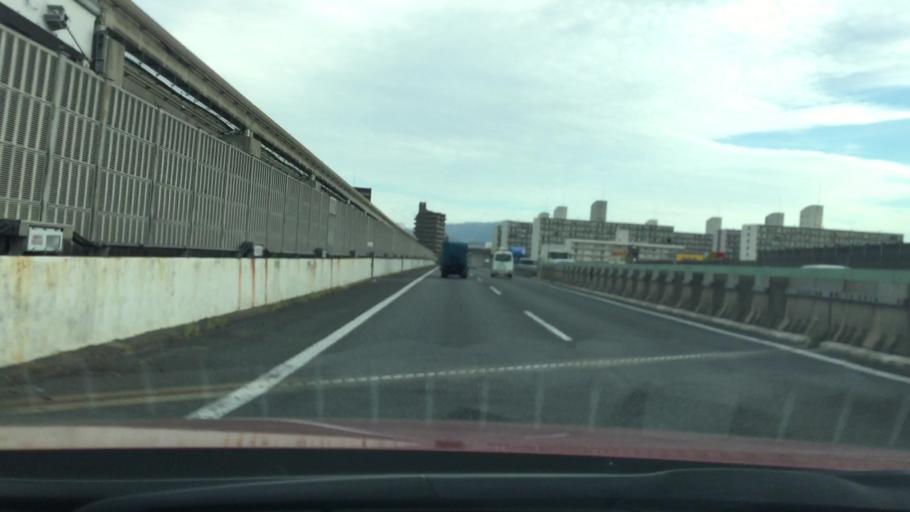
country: JP
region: Osaka
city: Ibaraki
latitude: 34.7956
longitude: 135.5661
